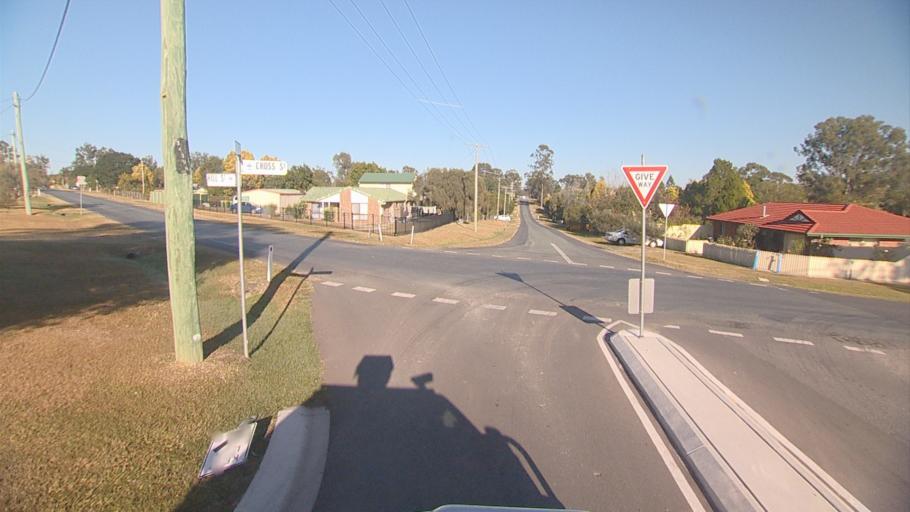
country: AU
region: Queensland
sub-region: Logan
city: Cedar Vale
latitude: -27.8316
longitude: 153.0321
